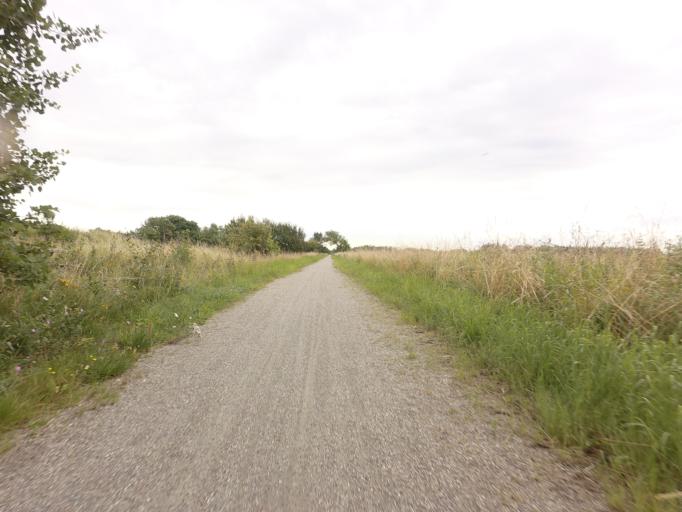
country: DK
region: North Denmark
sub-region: Alborg Kommune
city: Vadum
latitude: 57.0990
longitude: 9.8941
